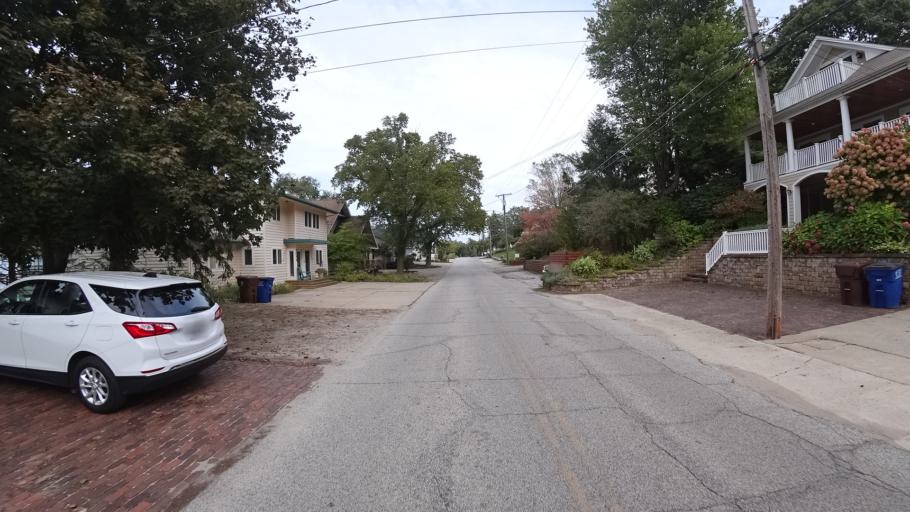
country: US
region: Indiana
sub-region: LaPorte County
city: Long Beach
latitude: 41.7433
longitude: -86.8615
